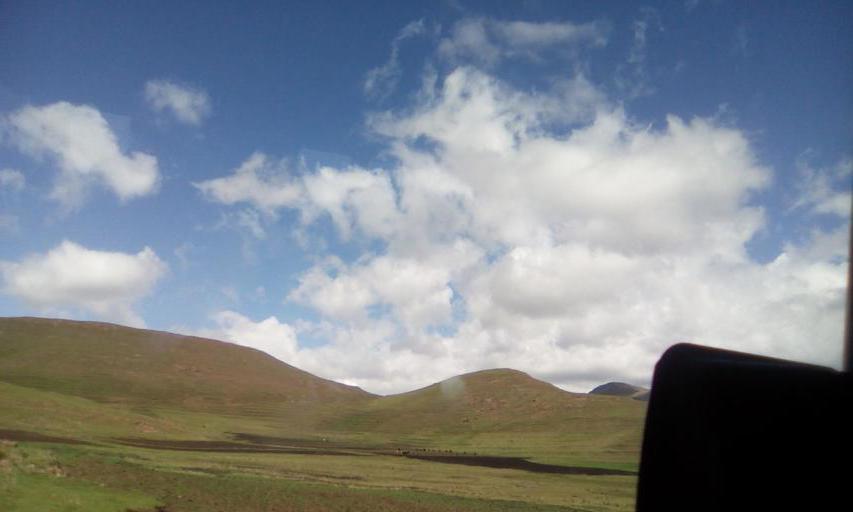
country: LS
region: Maseru
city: Nako
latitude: -29.8135
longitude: 28.0325
